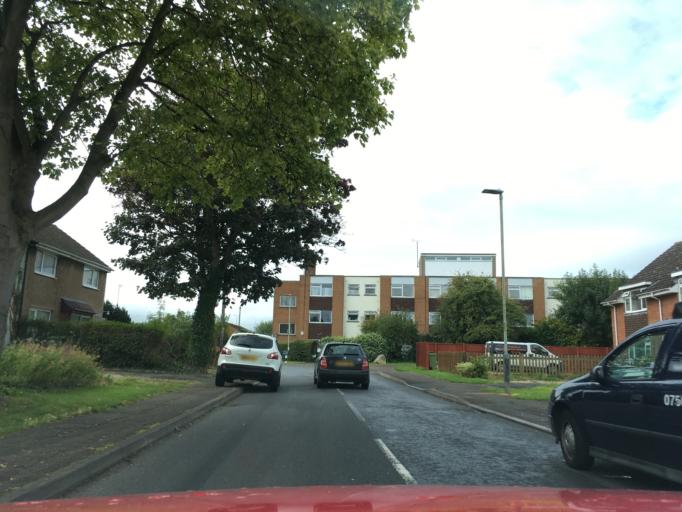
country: GB
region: England
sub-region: Gloucestershire
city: Uckington
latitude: 51.9056
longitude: -2.1219
